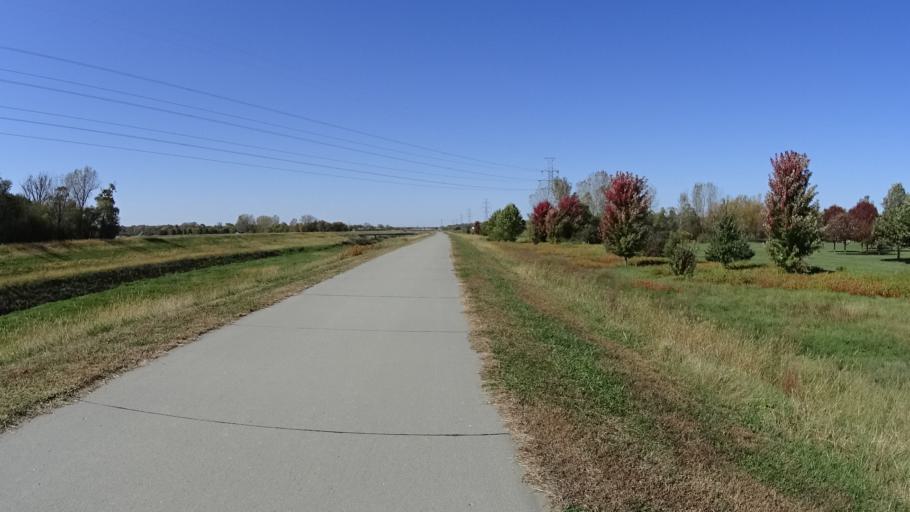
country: US
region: Nebraska
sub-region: Sarpy County
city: Papillion
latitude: 41.1511
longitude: -96.0085
